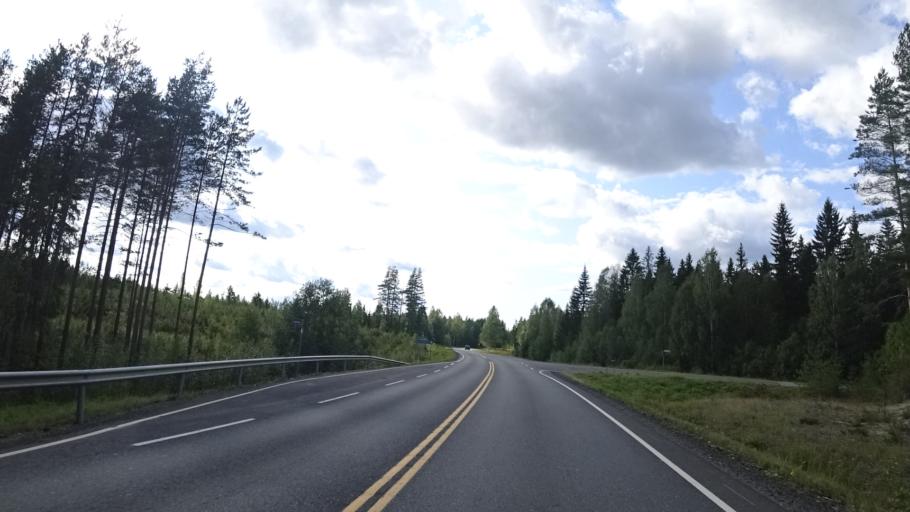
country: FI
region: North Karelia
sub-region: Keski-Karjala
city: Tohmajaervi
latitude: 62.1846
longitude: 30.5094
